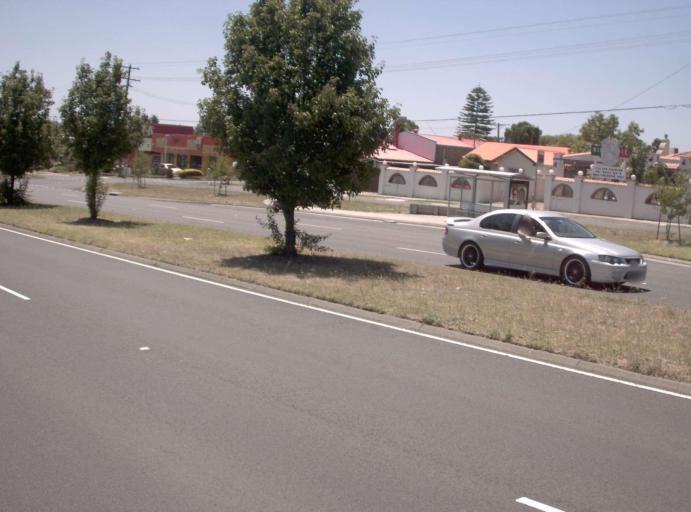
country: AU
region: Victoria
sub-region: Greater Dandenong
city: Springvale
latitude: -37.9355
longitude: 145.1591
